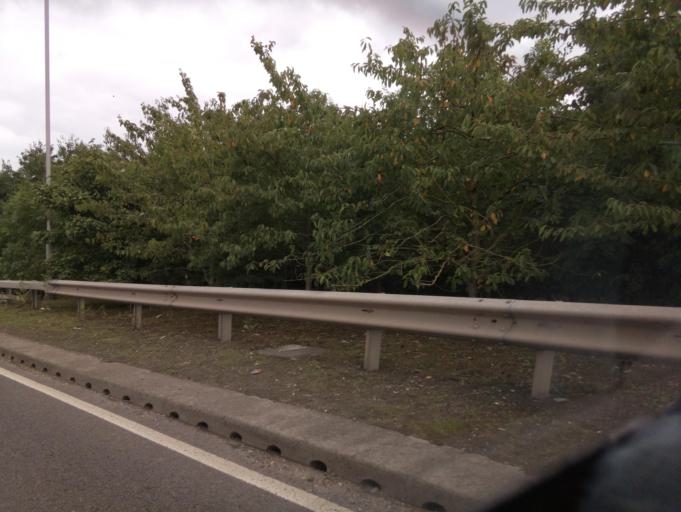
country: GB
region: England
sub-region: Nottinghamshire
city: Burton Joyce
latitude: 52.9723
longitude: -1.0602
